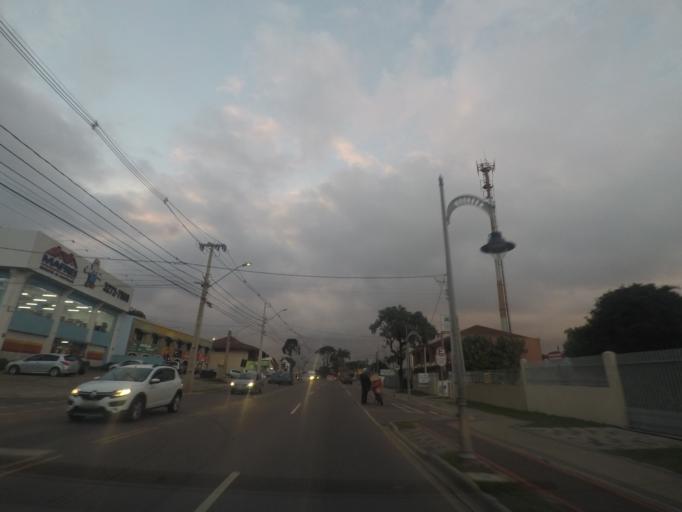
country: BR
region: Parana
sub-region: Almirante Tamandare
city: Almirante Tamandare
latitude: -25.3918
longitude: -49.3519
